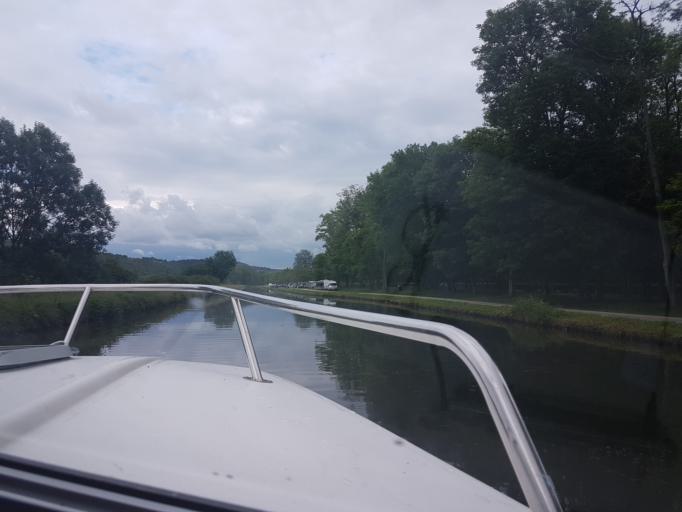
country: FR
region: Bourgogne
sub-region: Departement de l'Yonne
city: Saint-Bris-le-Vineux
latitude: 47.6965
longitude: 3.6450
